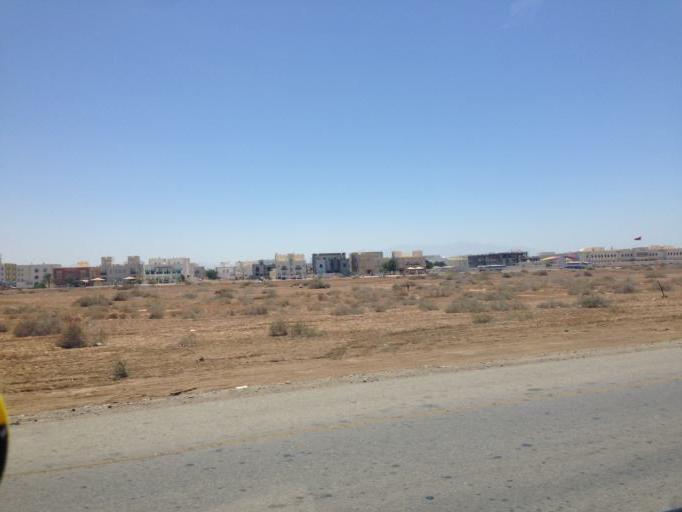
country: OM
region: Muhafazat Masqat
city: As Sib al Jadidah
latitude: 23.6285
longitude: 58.2573
